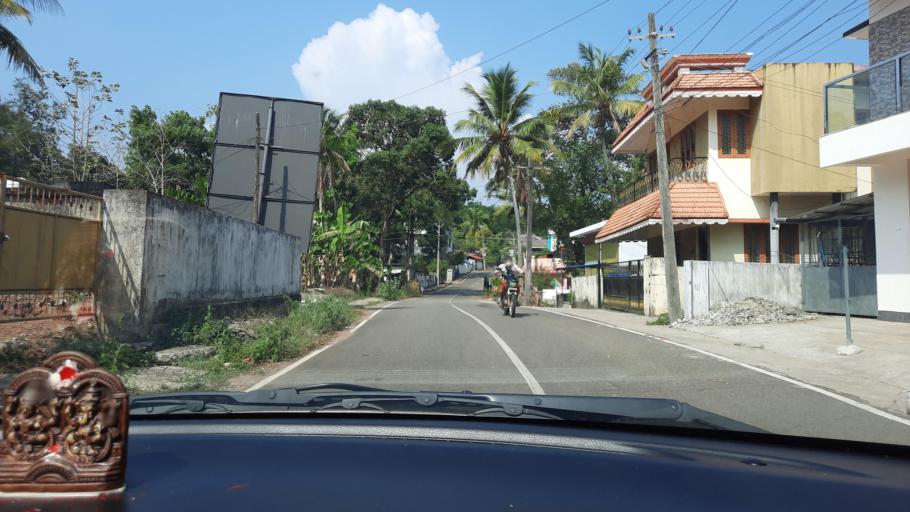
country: IN
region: Kerala
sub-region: Thiruvananthapuram
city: Nedumangad
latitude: 8.5866
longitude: 76.9258
